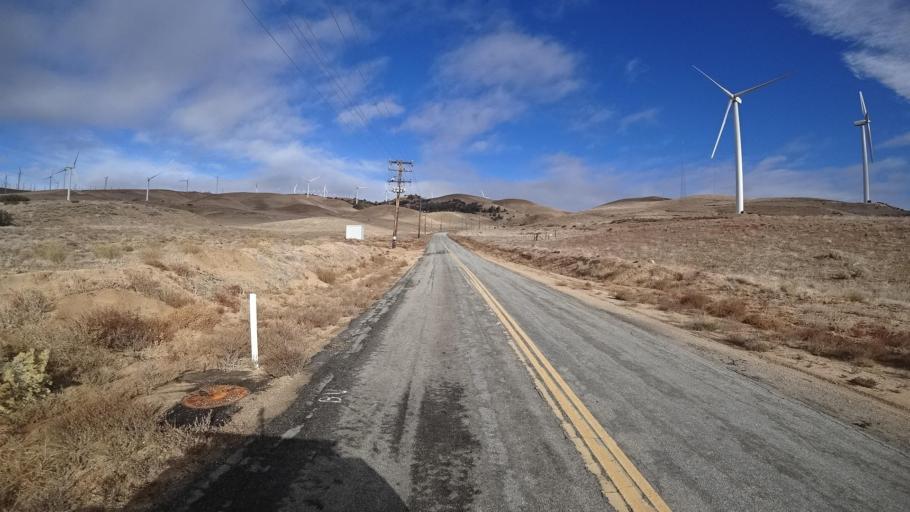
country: US
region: California
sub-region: Kern County
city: Tehachapi
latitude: 35.0596
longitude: -118.3532
